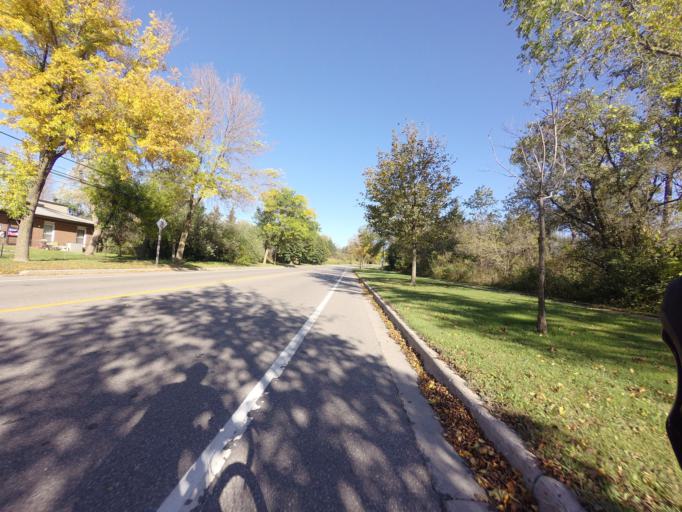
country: CA
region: Ontario
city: Oshawa
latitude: 43.8824
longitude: -78.8142
